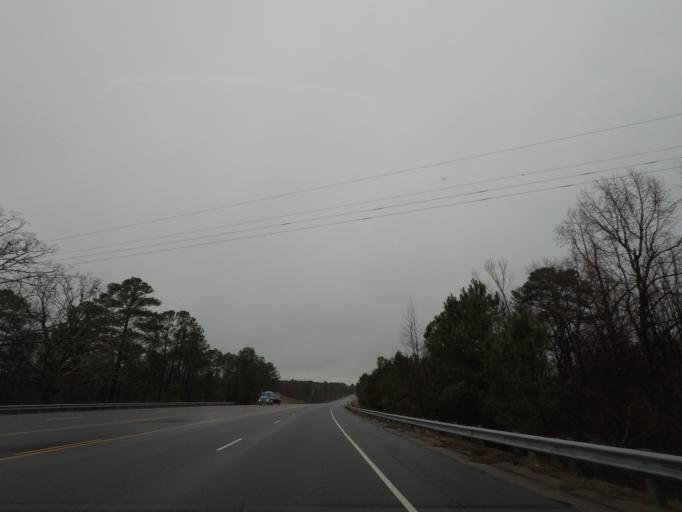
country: US
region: North Carolina
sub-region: Lee County
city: Broadway
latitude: 35.3452
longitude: -79.1062
